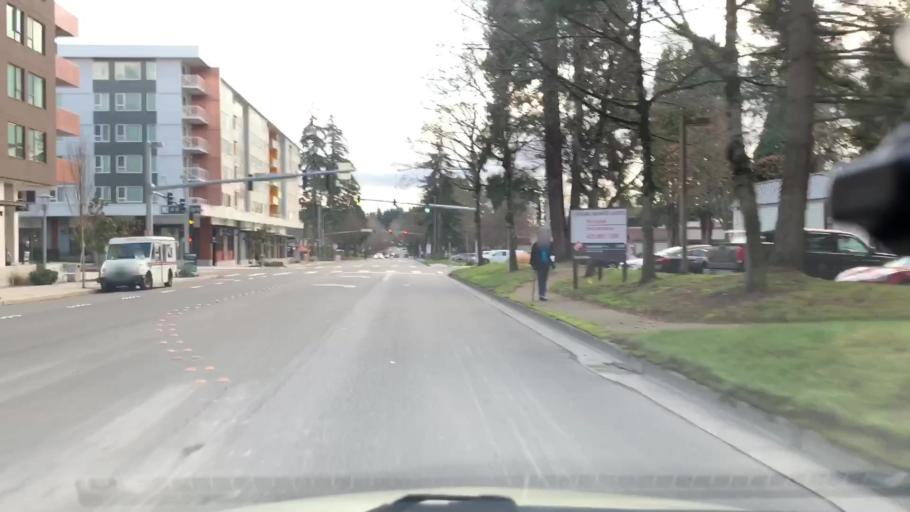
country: US
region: Washington
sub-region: King County
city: Redmond
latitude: 47.6348
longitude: -122.1377
